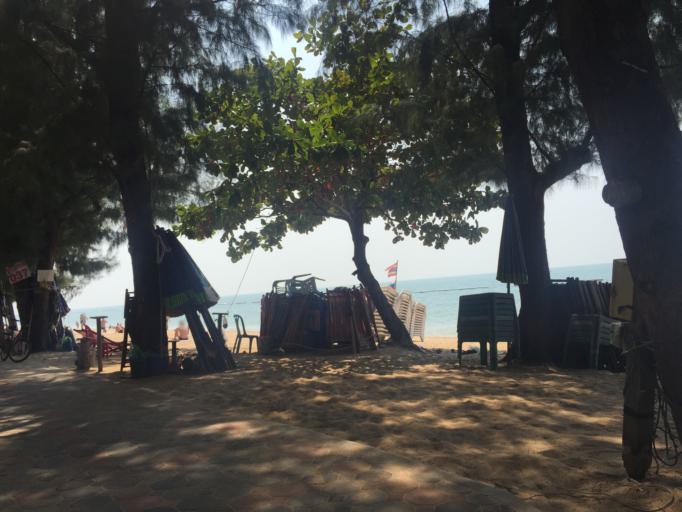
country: TH
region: Chon Buri
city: Phatthaya
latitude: 12.9041
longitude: 100.8614
